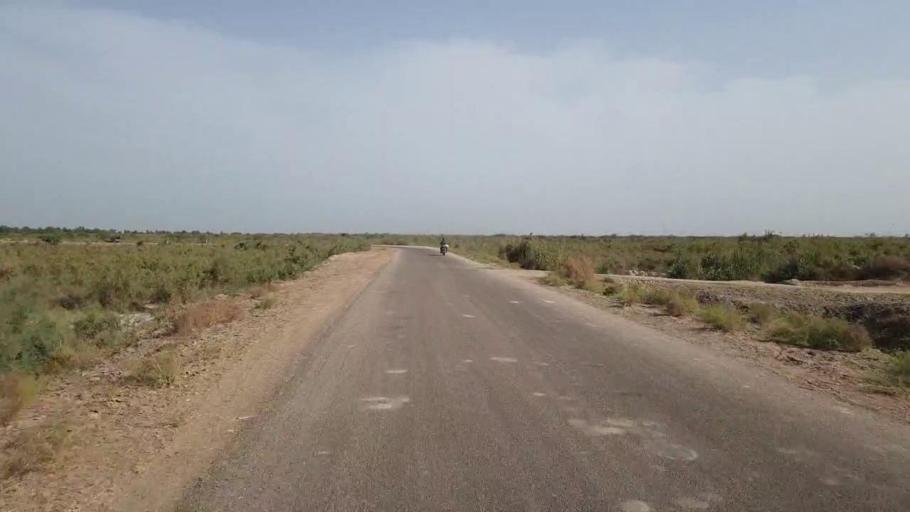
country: PK
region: Sindh
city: Sakrand
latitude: 26.2743
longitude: 68.2719
